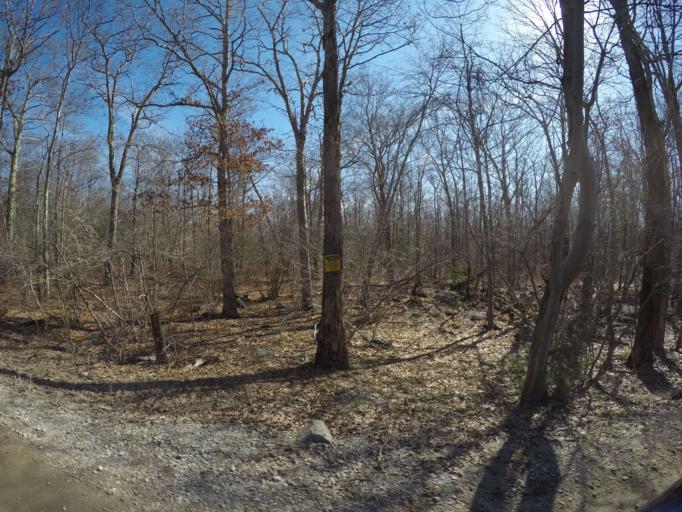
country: US
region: Massachusetts
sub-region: Norfolk County
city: Sharon
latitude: 42.0831
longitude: -71.1510
